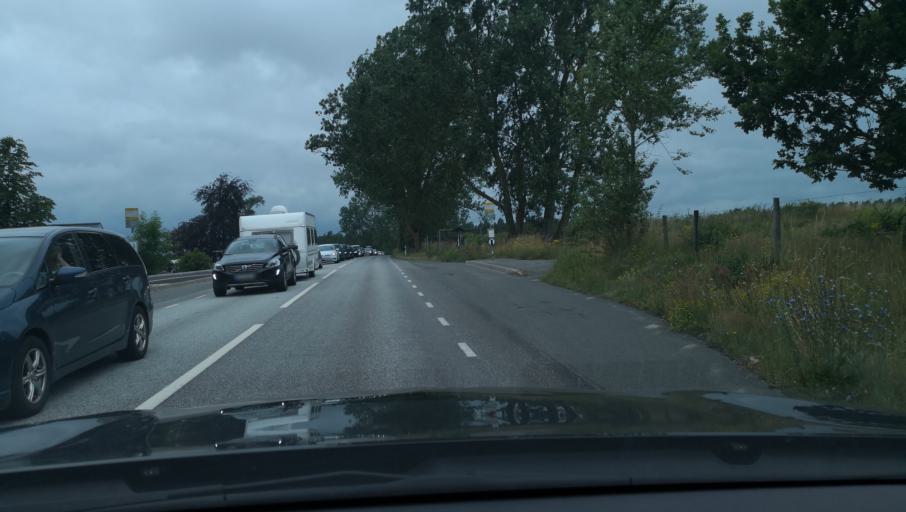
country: SE
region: Skane
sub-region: Simrishamns Kommun
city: Kivik
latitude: 55.7099
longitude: 14.1705
